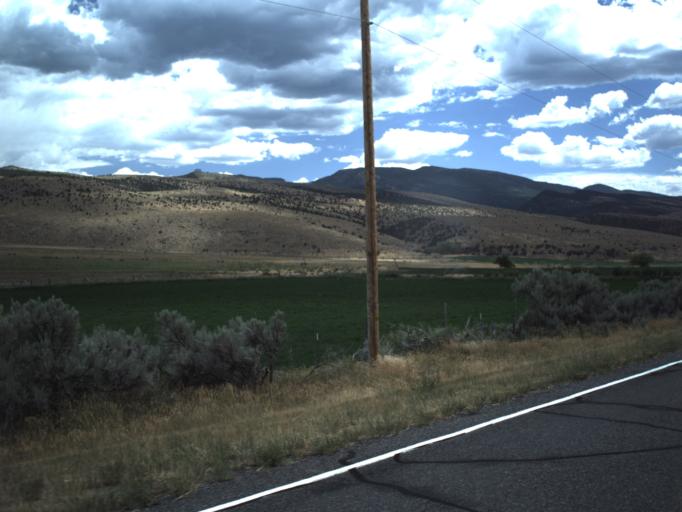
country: US
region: Utah
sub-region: Sanpete County
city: Gunnison
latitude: 39.1500
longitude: -111.7092
